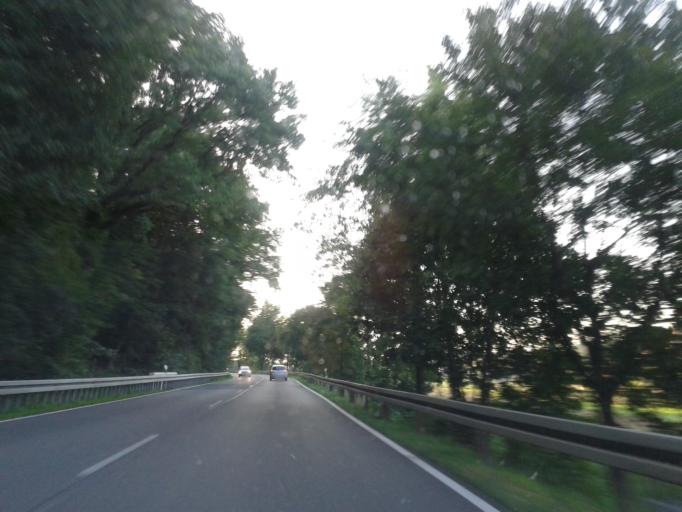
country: DE
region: Saxony
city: Meissen
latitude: 51.1826
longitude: 13.4498
